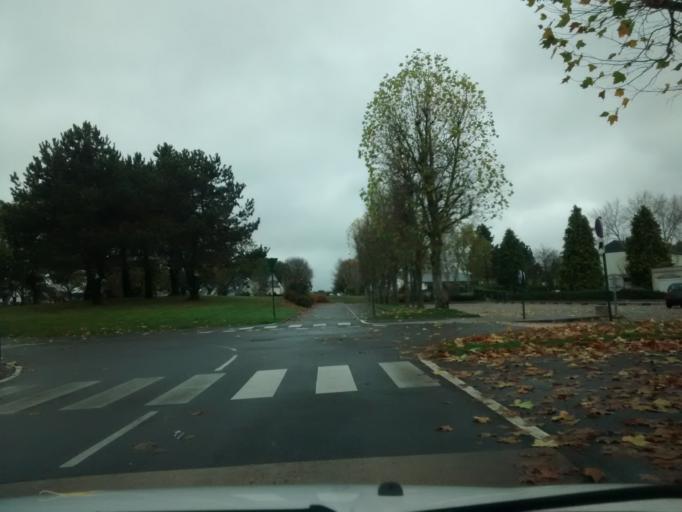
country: FR
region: Brittany
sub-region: Departement d'Ille-et-Vilaine
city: Cesson-Sevigne
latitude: 48.1232
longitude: -1.6007
